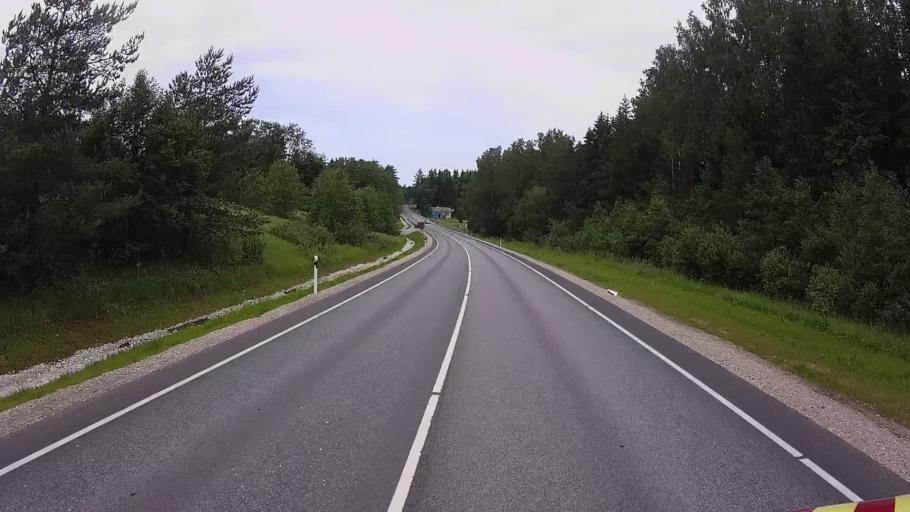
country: EE
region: Viljandimaa
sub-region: Viljandi linn
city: Viljandi
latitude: 58.2804
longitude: 25.5834
